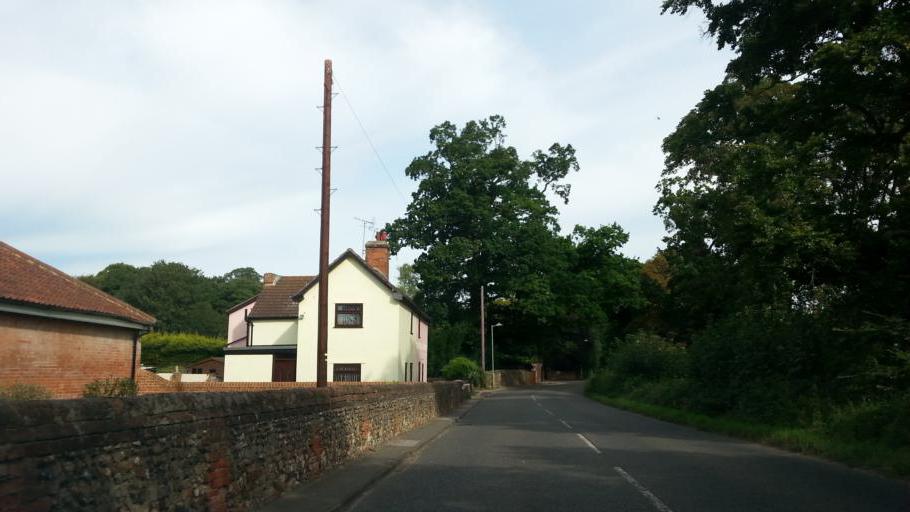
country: GB
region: England
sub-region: Suffolk
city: Bramford
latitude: 52.0557
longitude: 1.0966
